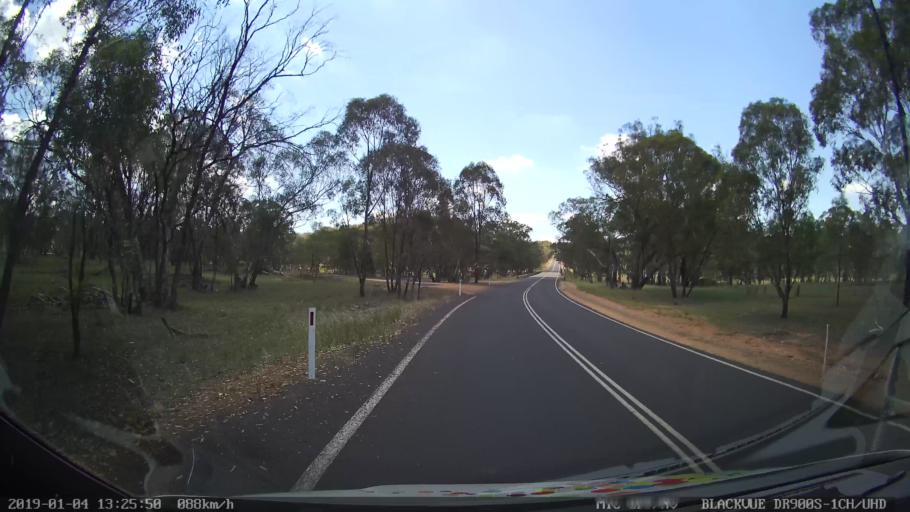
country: AU
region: New South Wales
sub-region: Parkes
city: Peak Hill
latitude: -32.6879
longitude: 148.5540
